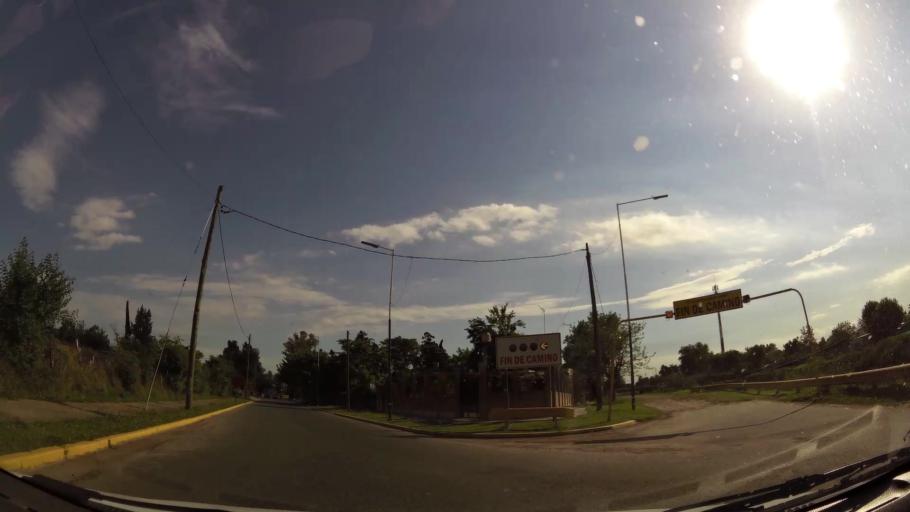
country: AR
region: Buenos Aires
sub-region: Partido de Merlo
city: Merlo
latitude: -34.6581
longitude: -58.7536
